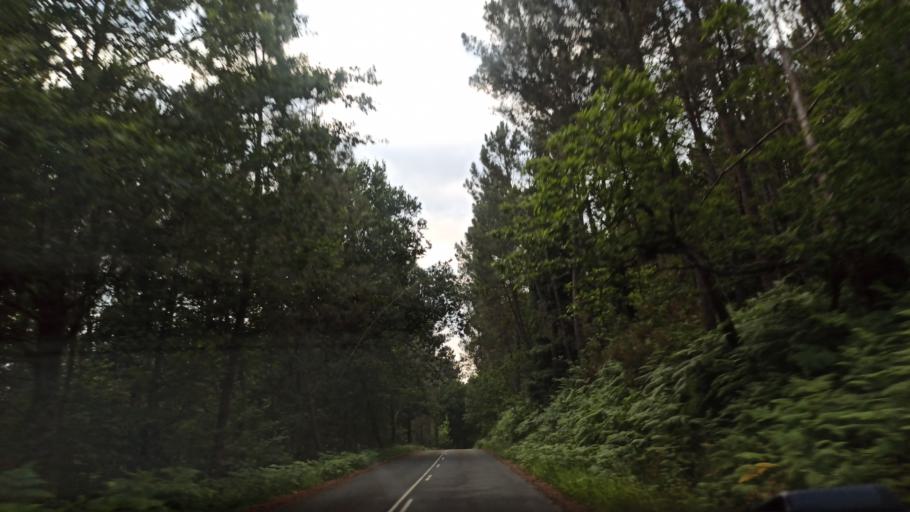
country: ES
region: Galicia
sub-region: Provincia da Coruna
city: Santiso
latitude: 42.8230
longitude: -8.1249
